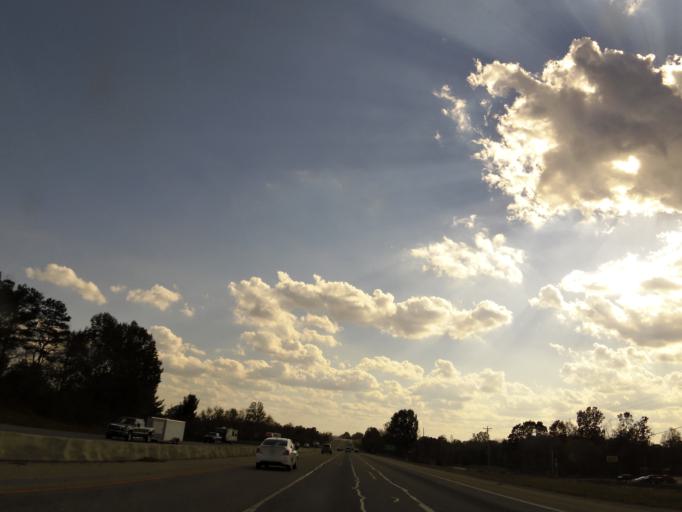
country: US
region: Kentucky
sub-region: Laurel County
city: London
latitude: 37.0808
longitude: -84.0995
